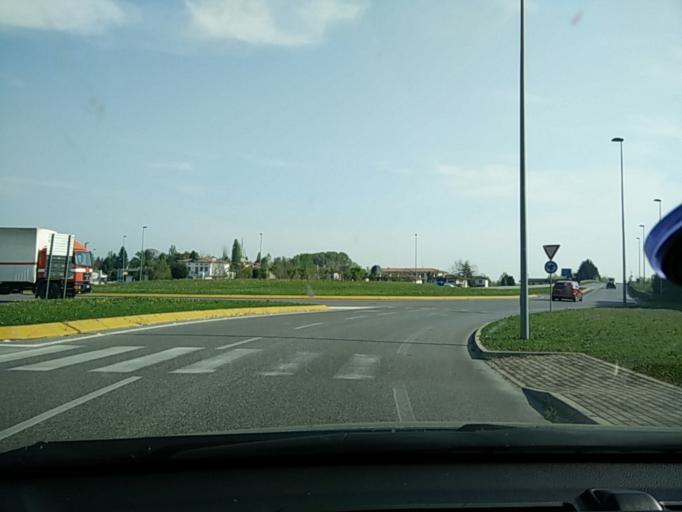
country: IT
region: Friuli Venezia Giulia
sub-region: Provincia di Pordenone
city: Prata di Sotto
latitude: 45.8966
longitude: 12.5998
